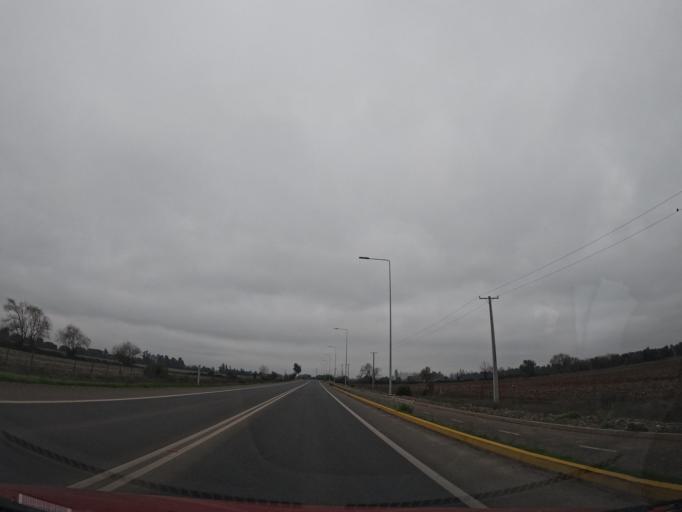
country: CL
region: Maule
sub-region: Provincia de Talca
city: San Clemente
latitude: -35.5110
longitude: -71.5062
